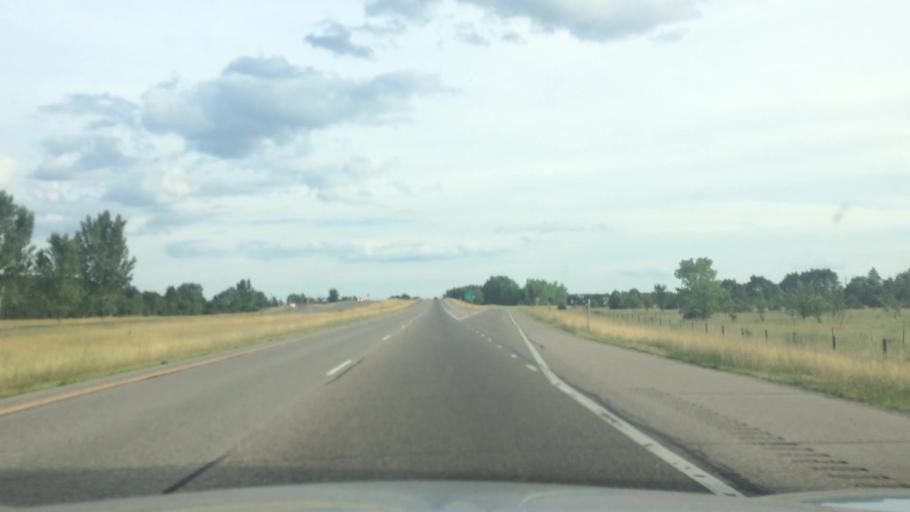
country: US
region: Wisconsin
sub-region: Portage County
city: Plover
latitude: 44.2192
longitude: -89.5248
